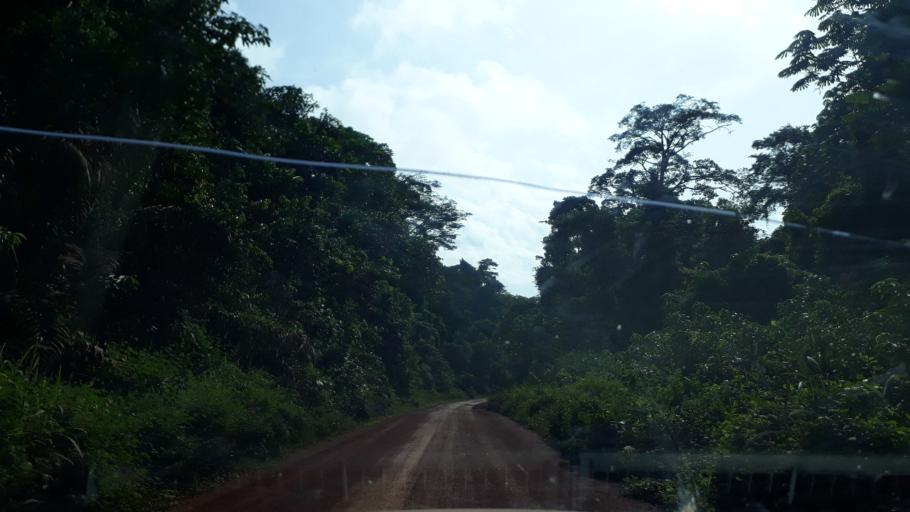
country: CD
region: Eastern Province
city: Wamba
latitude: 1.4204
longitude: 27.7925
